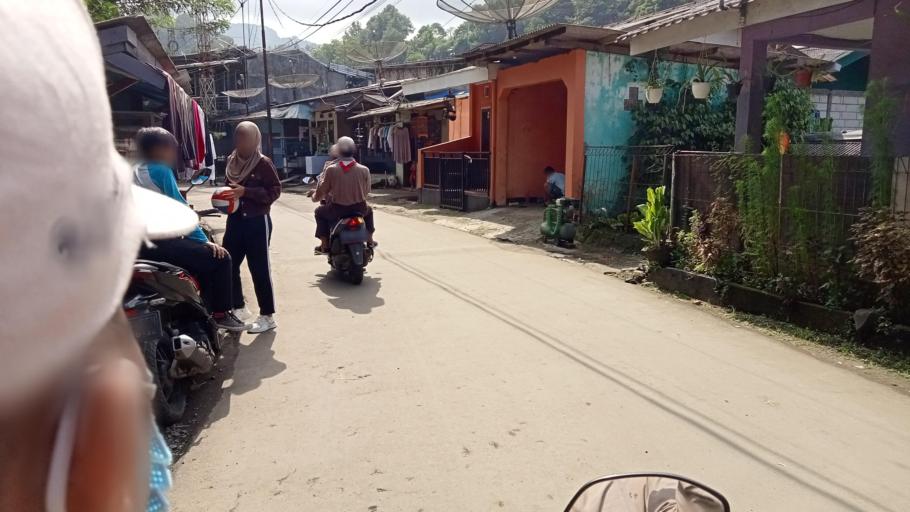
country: ID
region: West Java
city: Caringin
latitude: -6.6464
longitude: 106.9087
